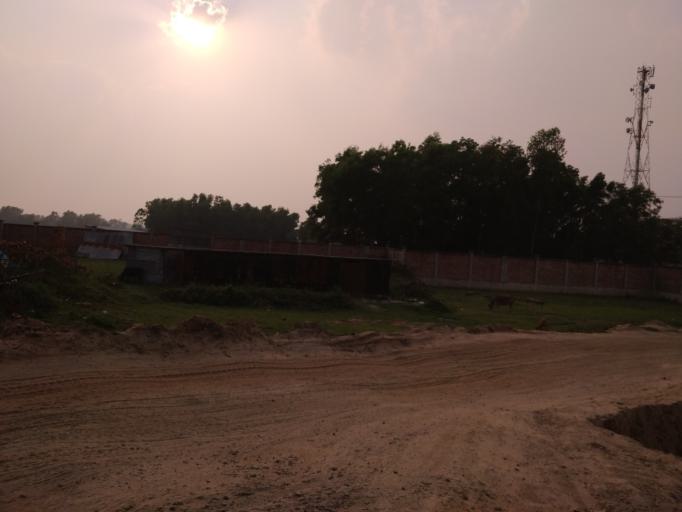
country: BD
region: Sylhet
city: Habiganj
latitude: 24.1481
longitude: 91.3514
